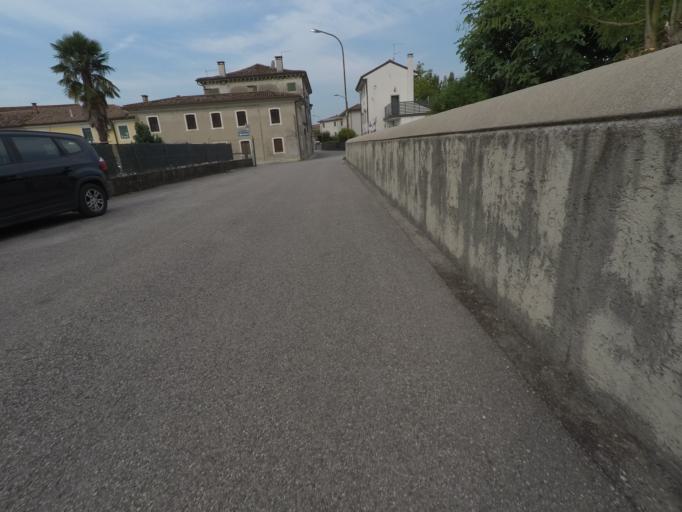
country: IT
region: Veneto
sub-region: Provincia di Treviso
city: Scomigo
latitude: 45.9653
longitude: 12.3283
